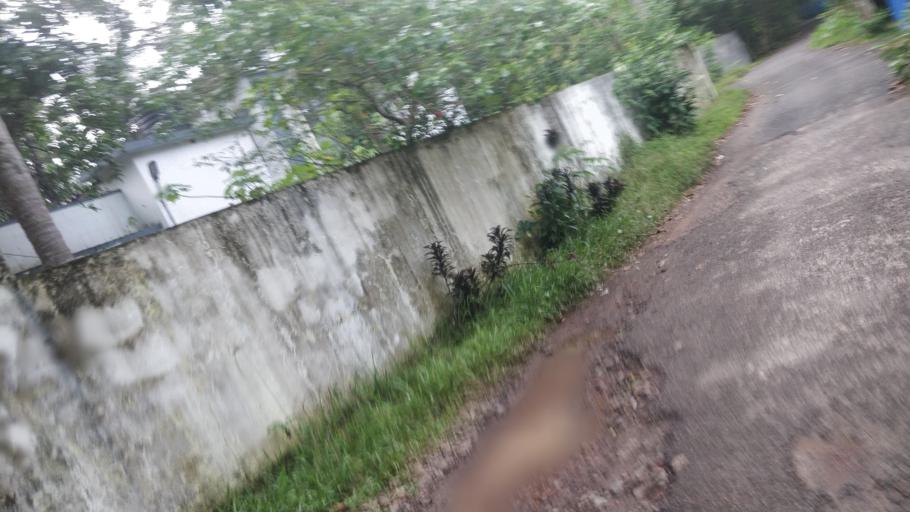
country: IN
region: Kerala
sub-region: Alappuzha
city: Shertallai
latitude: 9.6871
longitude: 76.3566
